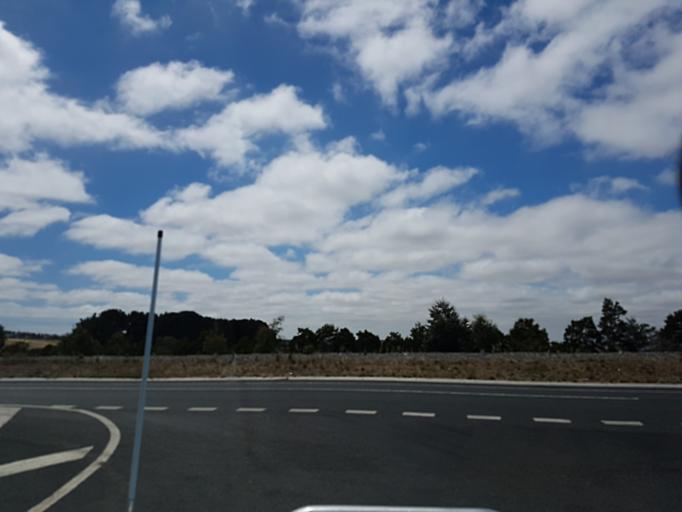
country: AU
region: Victoria
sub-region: Greater Geelong
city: Wandana Heights
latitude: -38.2137
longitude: 144.1806
